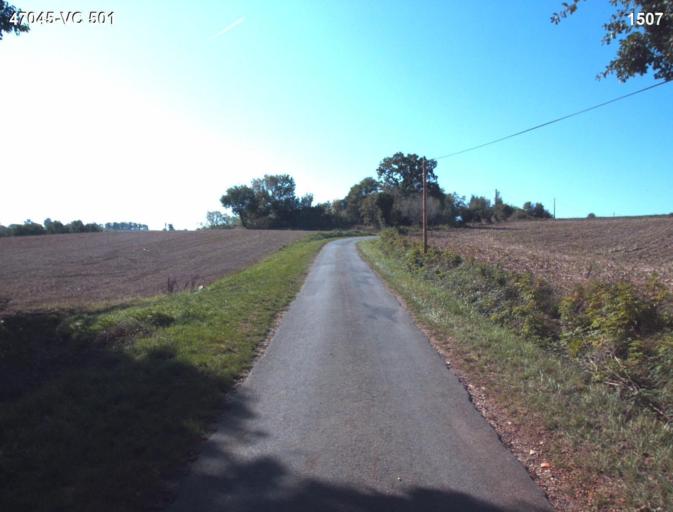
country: FR
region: Aquitaine
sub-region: Departement du Lot-et-Garonne
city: Nerac
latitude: 44.1619
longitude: 0.4141
